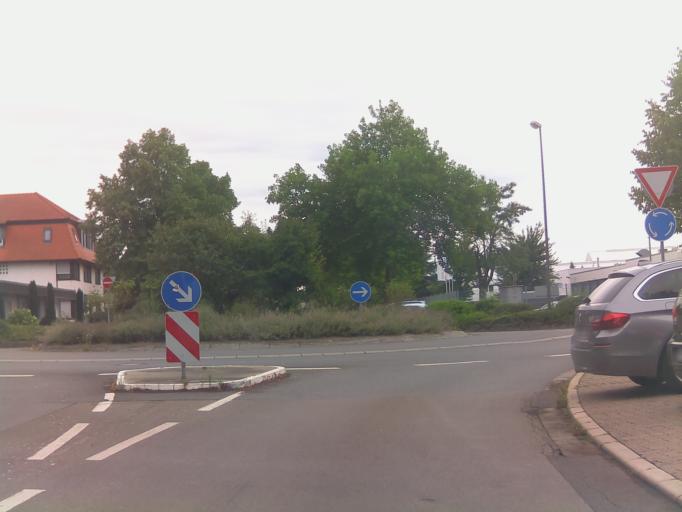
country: DE
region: Baden-Wuerttemberg
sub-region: Karlsruhe Region
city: Leimen
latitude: 49.3654
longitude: 8.6797
